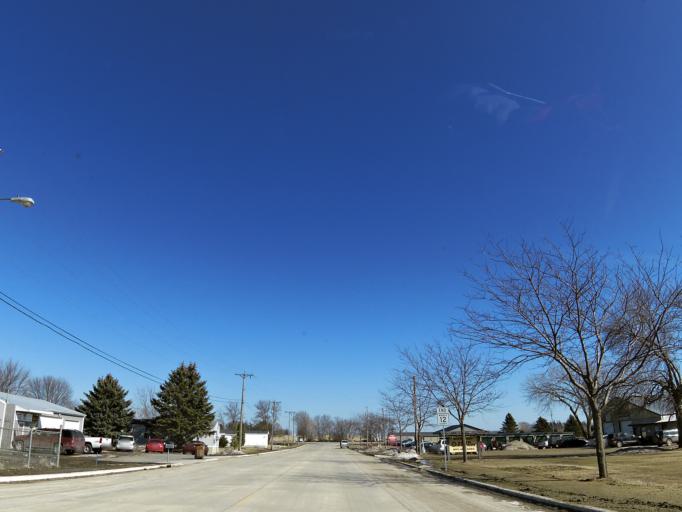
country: US
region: Minnesota
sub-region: Waseca County
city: New Richland
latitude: 43.8971
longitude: -93.4894
